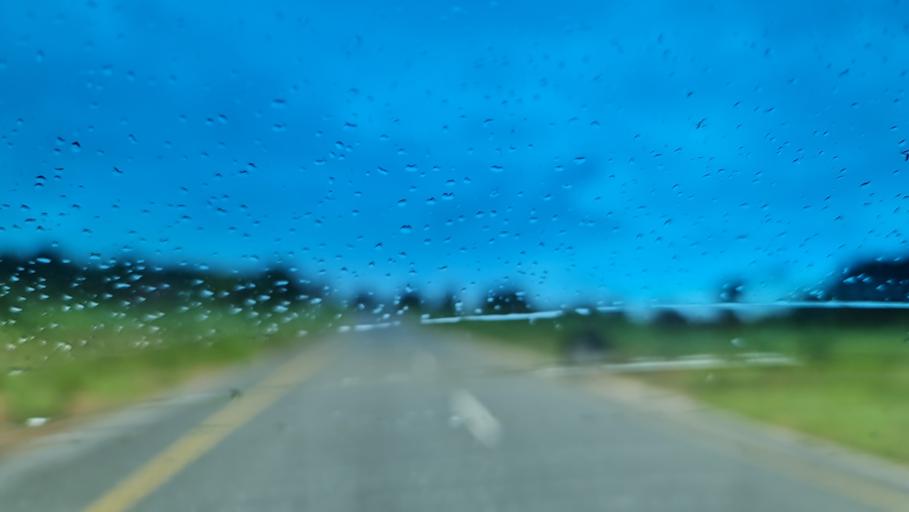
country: MZ
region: Nampula
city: Nampula
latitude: -15.4975
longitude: 39.3322
